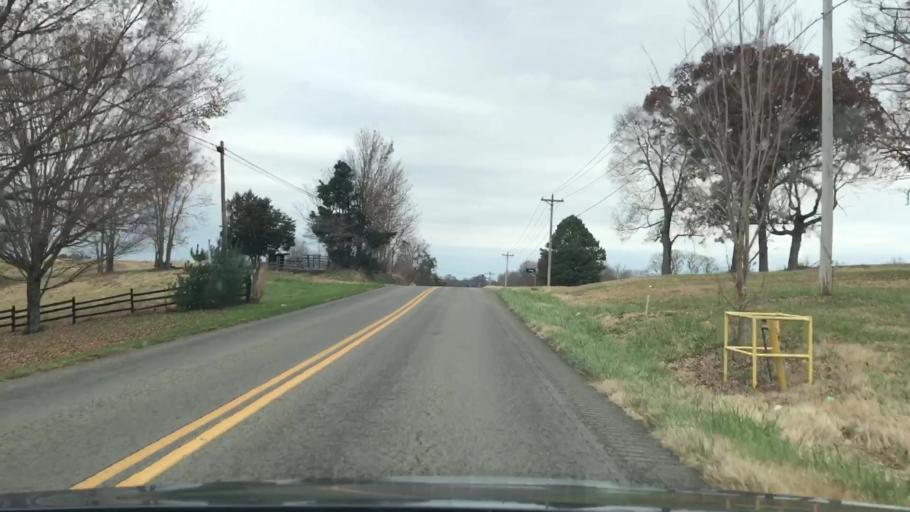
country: US
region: Kentucky
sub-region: Metcalfe County
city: Edmonton
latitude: 36.9524
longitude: -85.6146
